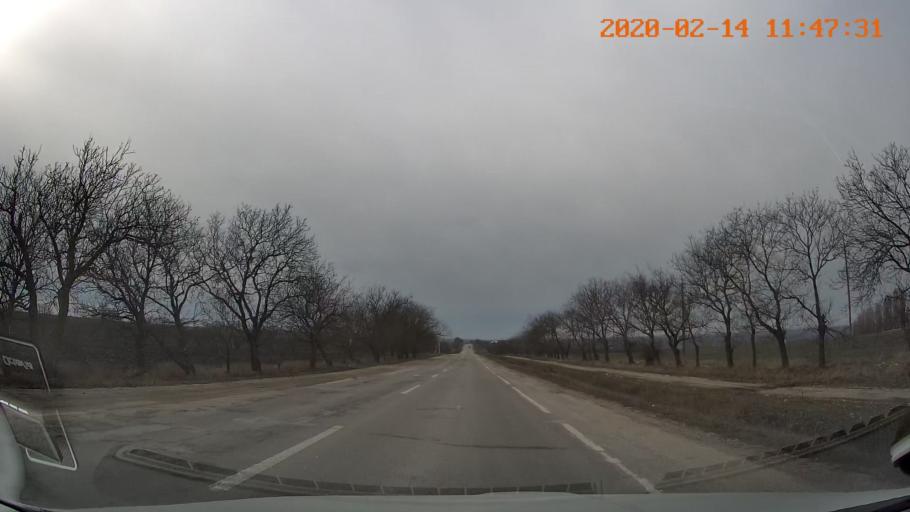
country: MD
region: Briceni
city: Briceni
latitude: 48.3156
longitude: 26.9683
